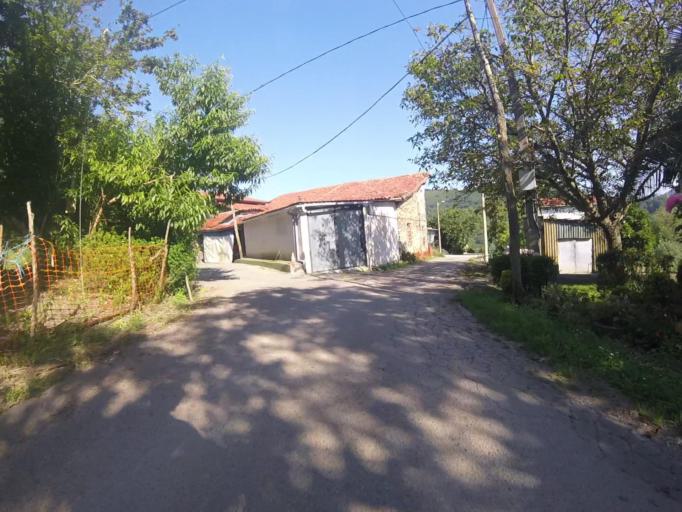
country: ES
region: Basque Country
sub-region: Provincia de Guipuzcoa
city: Astigarraga
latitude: 43.2572
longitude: -1.9411
